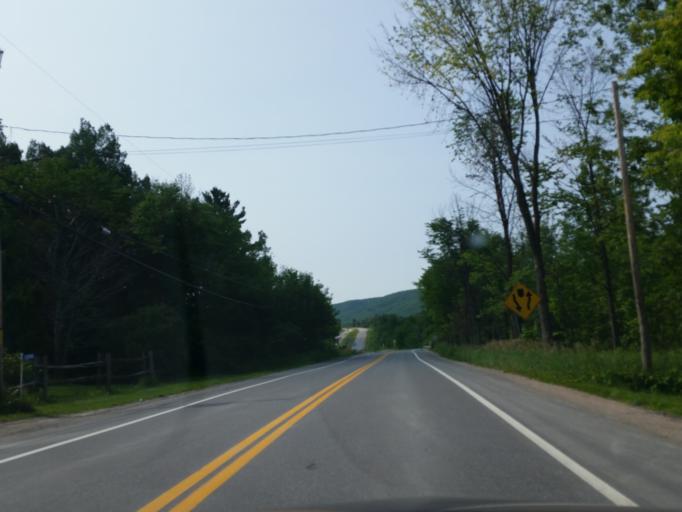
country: CA
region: Quebec
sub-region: Outaouais
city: Wakefield
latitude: 45.5066
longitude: -75.9721
